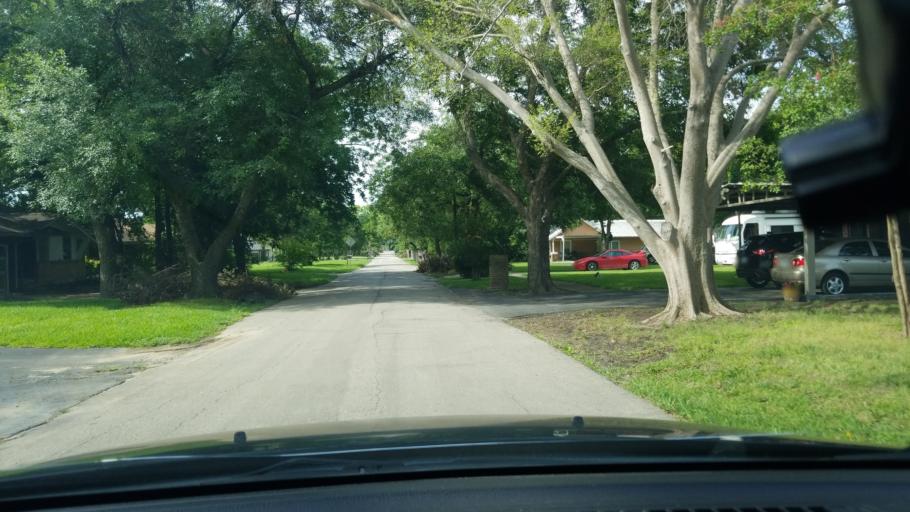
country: US
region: Texas
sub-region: Dallas County
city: Balch Springs
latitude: 32.7670
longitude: -96.6647
